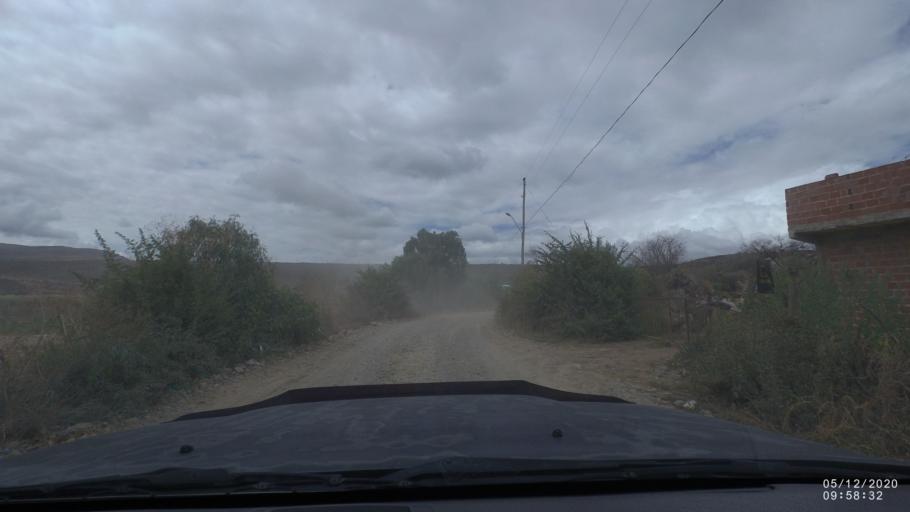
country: BO
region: Cochabamba
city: Sipe Sipe
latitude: -17.4299
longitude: -66.2919
